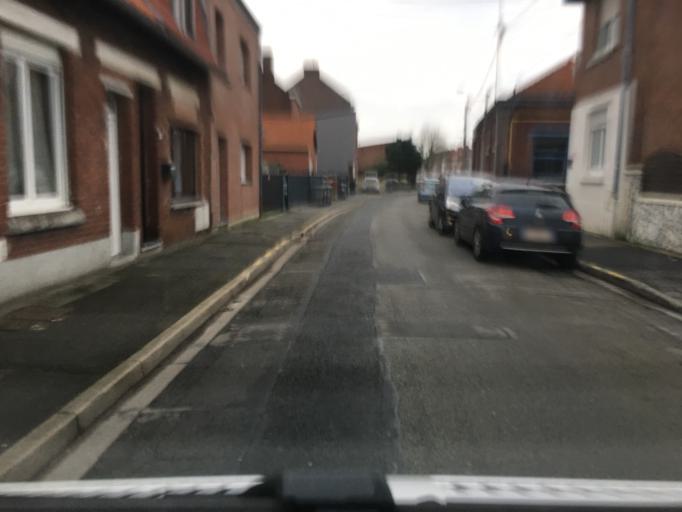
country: FR
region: Nord-Pas-de-Calais
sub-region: Departement du Nord
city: Comines
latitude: 50.7589
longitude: 3.0082
